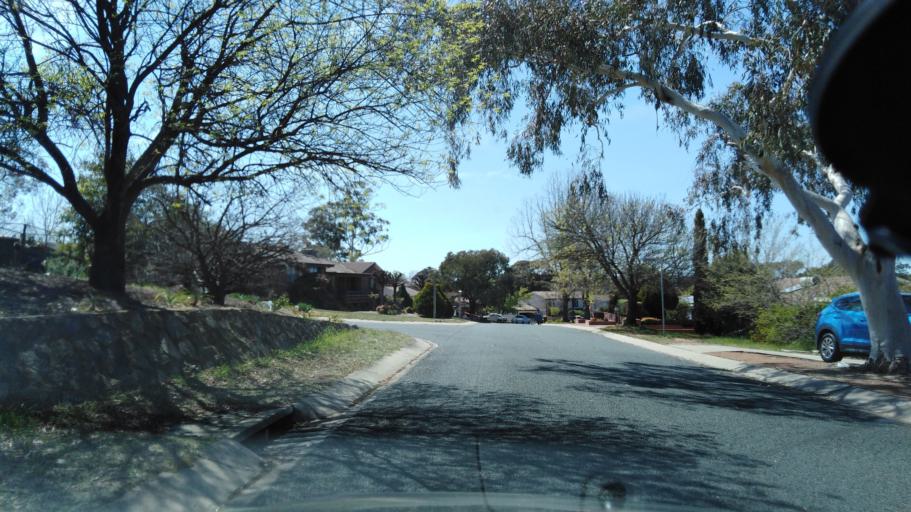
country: AU
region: Australian Capital Territory
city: Forrest
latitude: -35.3500
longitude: 149.0346
